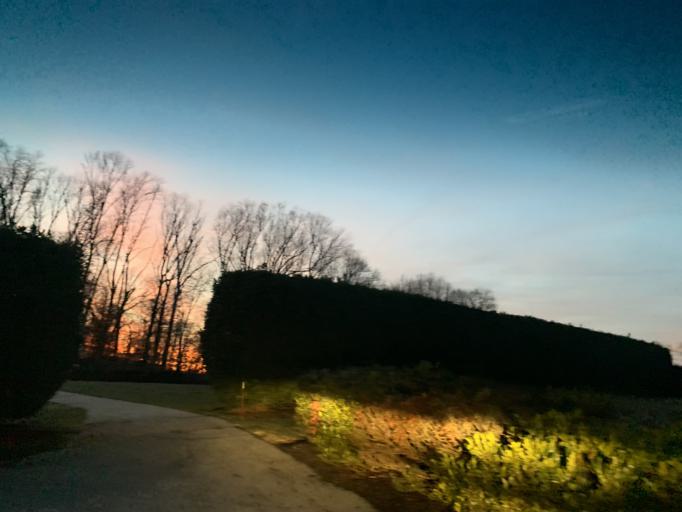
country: US
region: Maryland
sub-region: Baltimore County
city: Carney
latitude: 39.4487
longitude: -76.5193
